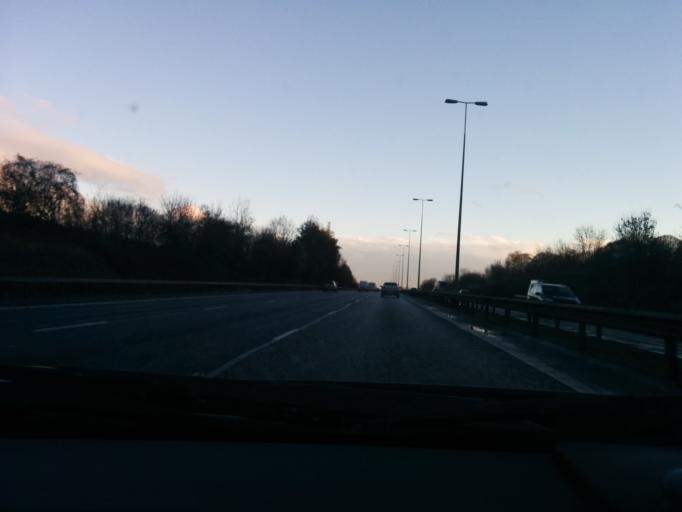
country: GB
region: England
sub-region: Buckinghamshire
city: Marlow
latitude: 51.6213
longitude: -0.8173
